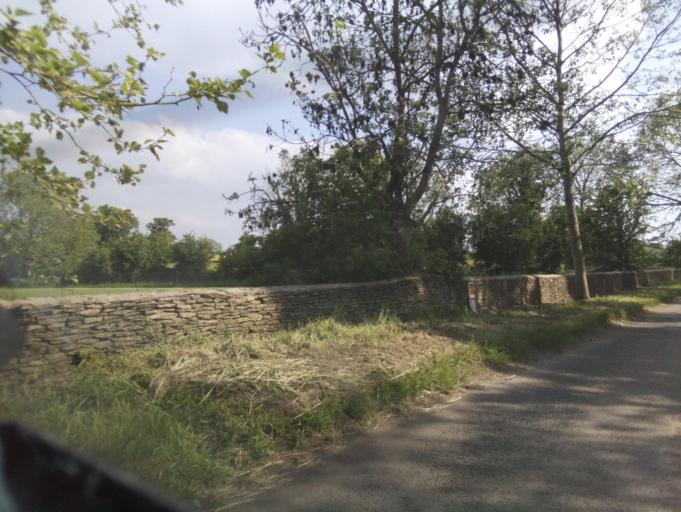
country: GB
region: England
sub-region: Wiltshire
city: Luckington
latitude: 51.5843
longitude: -2.2677
